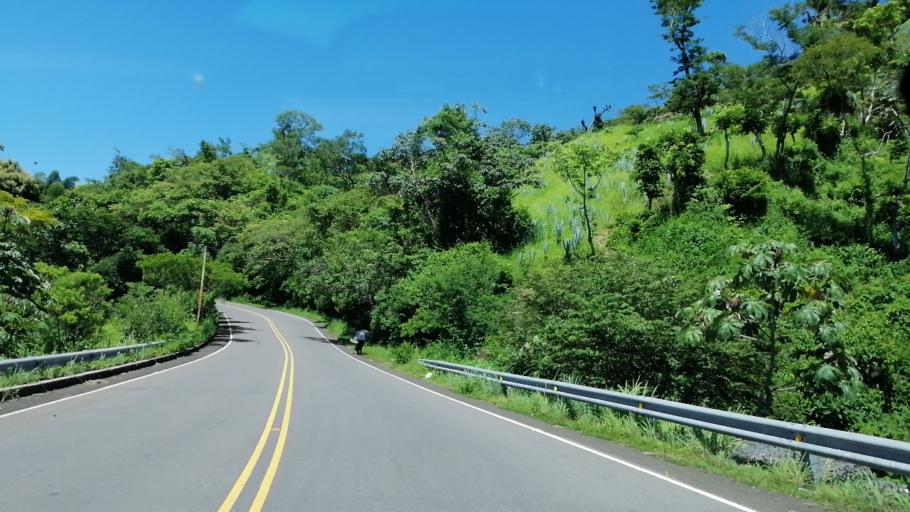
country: SV
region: San Miguel
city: Ciudad Barrios
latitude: 13.8121
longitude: -88.1775
